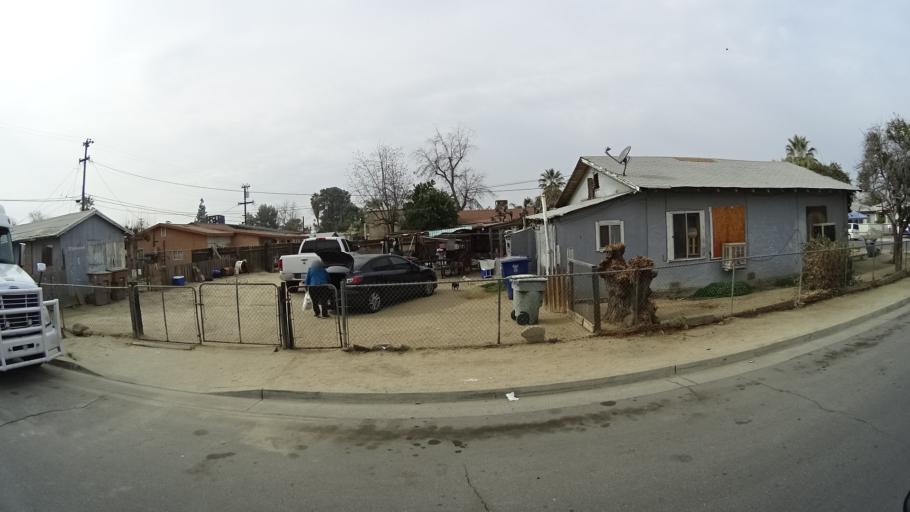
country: US
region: California
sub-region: Kern County
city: Bakersfield
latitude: 35.3623
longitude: -118.9990
